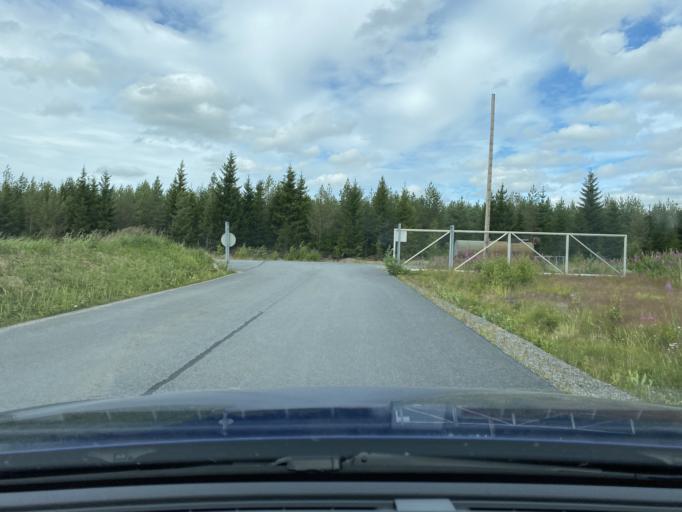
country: FI
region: Southern Ostrobothnia
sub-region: Seinaejoki
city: Jurva
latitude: 62.6240
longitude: 22.0328
